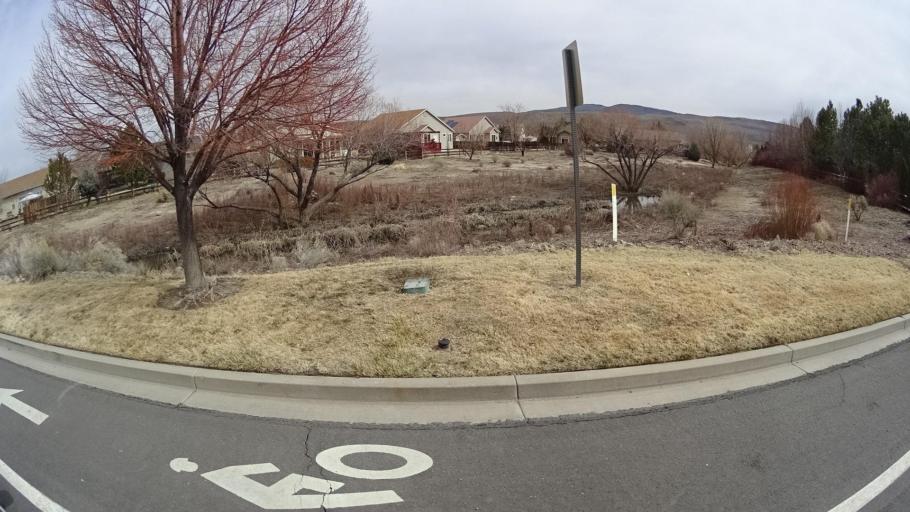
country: US
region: Nevada
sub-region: Washoe County
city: Spanish Springs
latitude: 39.6289
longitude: -119.6893
